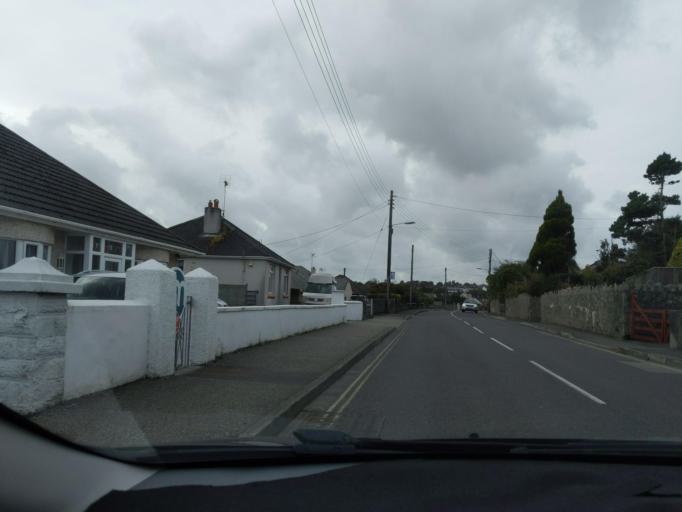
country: GB
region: England
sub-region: Cornwall
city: St Austell
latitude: 50.3439
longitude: -4.7645
